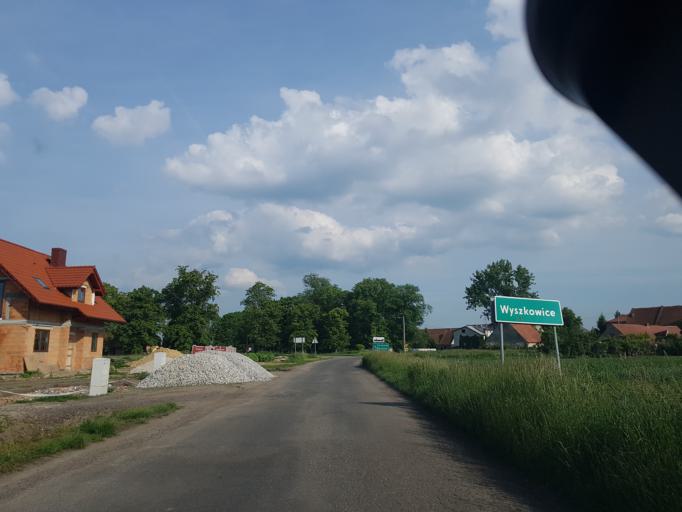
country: PL
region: Lower Silesian Voivodeship
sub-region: Powiat olawski
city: Wierzbno
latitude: 50.8702
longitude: 17.1553
